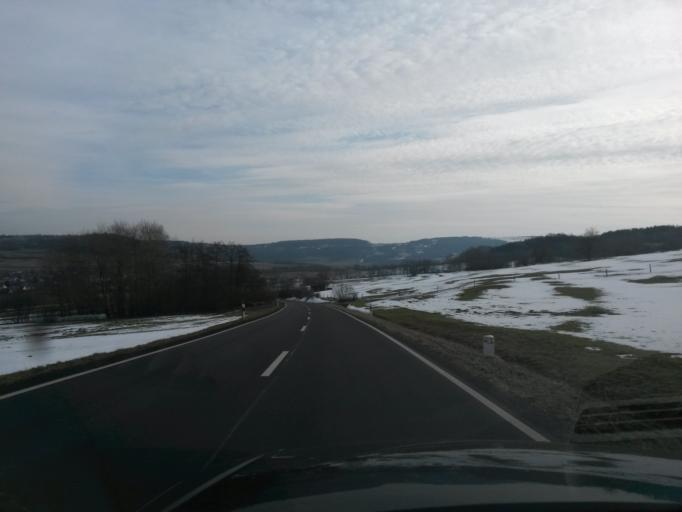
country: DE
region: Hesse
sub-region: Regierungsbezirk Kassel
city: Hilders
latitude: 50.5836
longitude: 10.0180
